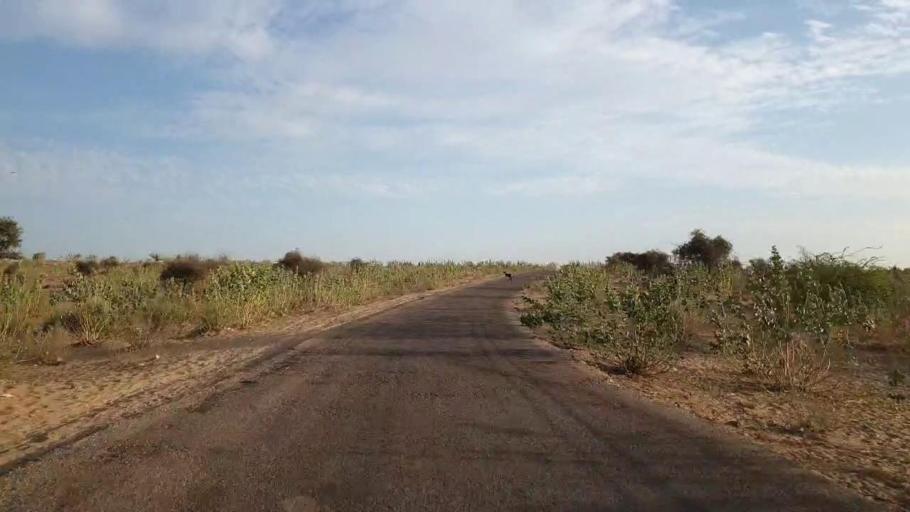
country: PK
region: Sindh
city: Umarkot
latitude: 25.1498
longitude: 70.0132
